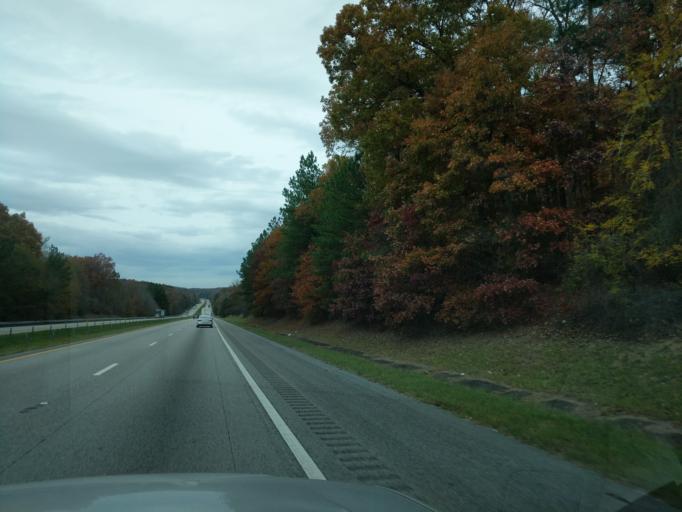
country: US
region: South Carolina
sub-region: Laurens County
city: Clinton
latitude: 34.5814
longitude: -81.8932
